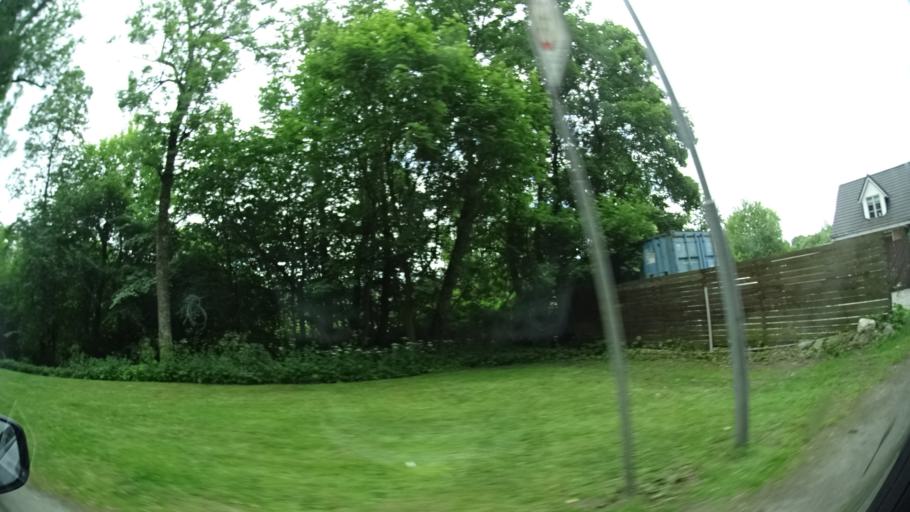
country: DK
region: Central Jutland
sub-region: Syddjurs Kommune
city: Ryomgard
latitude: 56.4074
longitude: 10.5648
